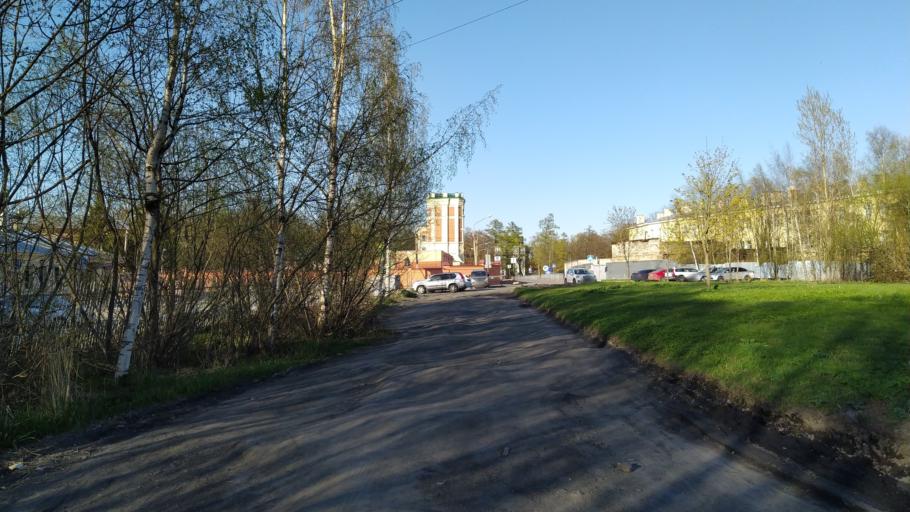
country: RU
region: St.-Petersburg
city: Pushkin
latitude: 59.7085
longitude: 30.3779
